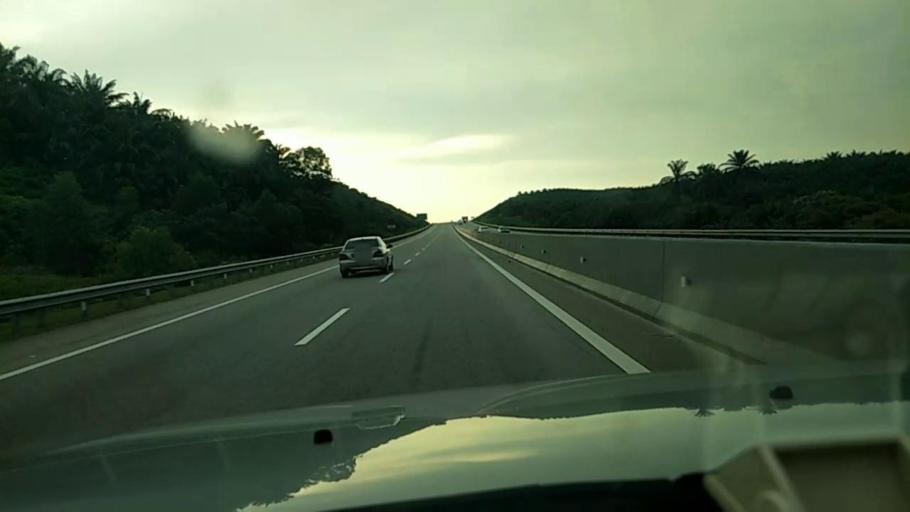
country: MY
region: Selangor
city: Batu Arang
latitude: 3.2795
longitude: 101.4491
